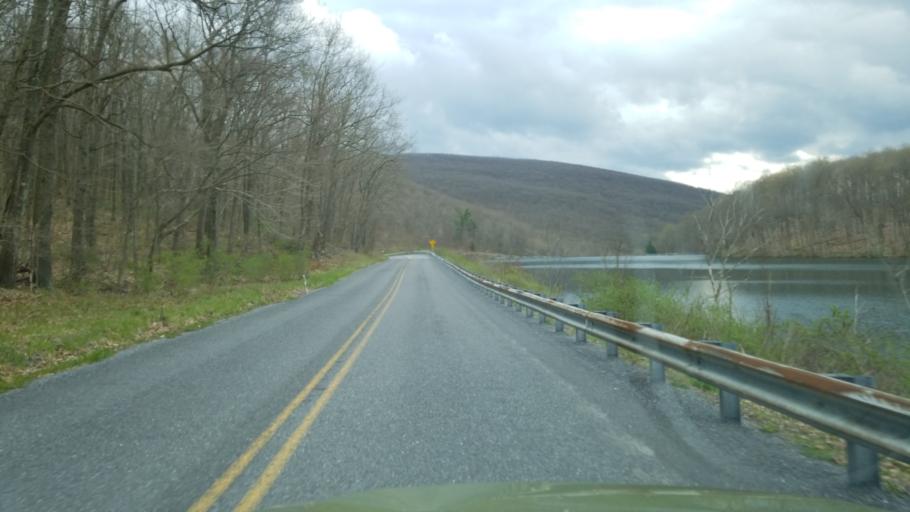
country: US
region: Pennsylvania
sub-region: Blair County
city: Tipton
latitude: 40.6803
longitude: -78.3279
